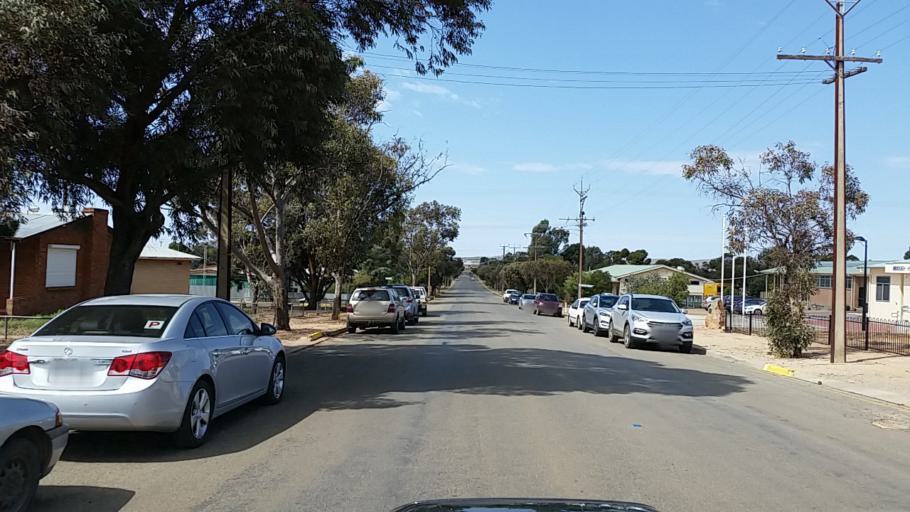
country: AU
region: South Australia
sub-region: Peterborough
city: Peterborough
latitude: -32.9781
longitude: 138.8355
